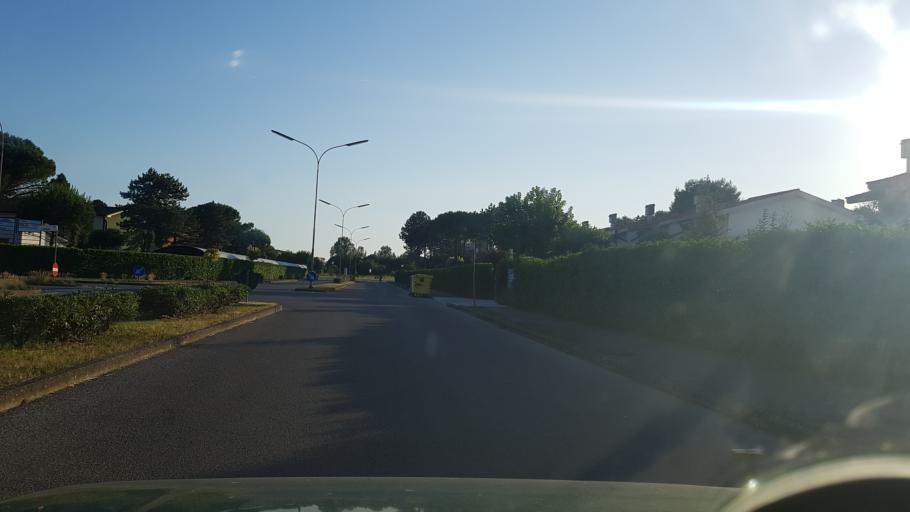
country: IT
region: Veneto
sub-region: Provincia di Venezia
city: Bibione
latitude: 45.6416
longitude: 13.0421
